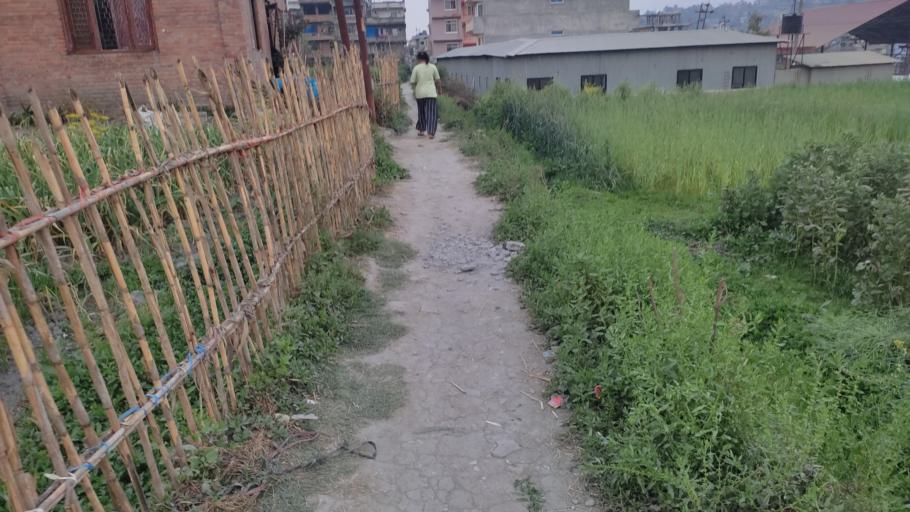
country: NP
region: Central Region
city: Kirtipur
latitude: 27.6681
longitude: 85.2775
